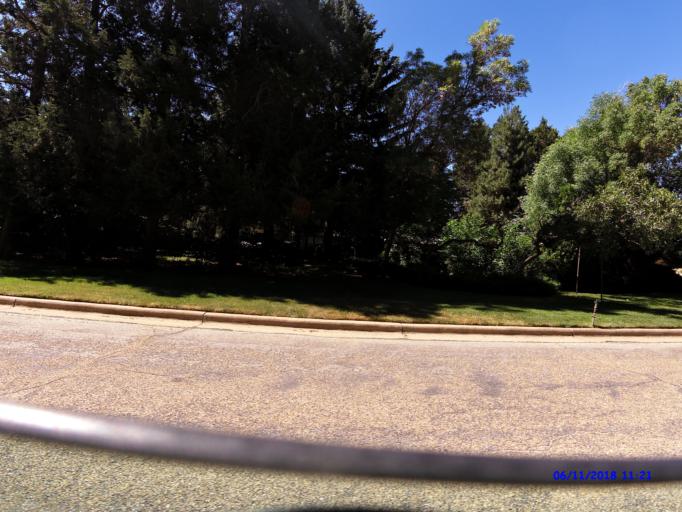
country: US
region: Utah
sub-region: Weber County
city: Ogden
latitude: 41.2233
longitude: -111.9338
